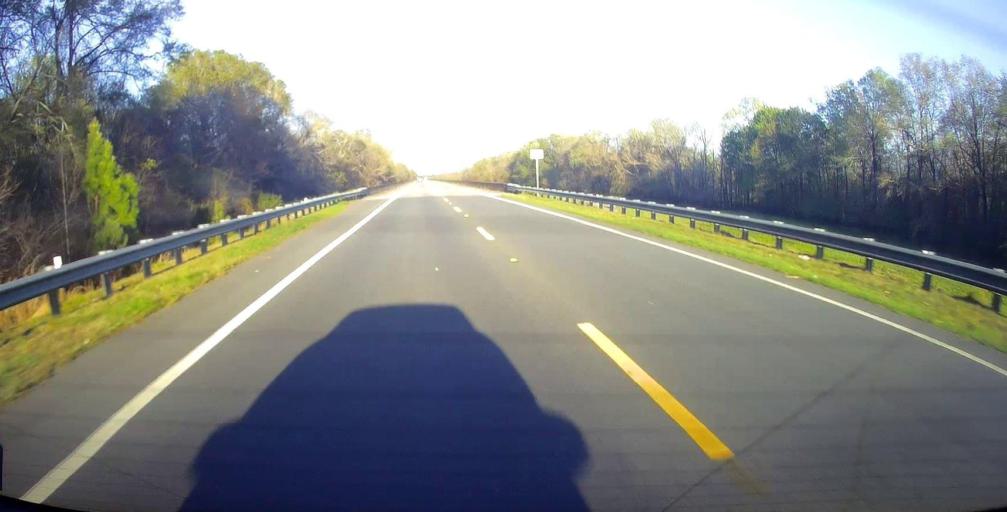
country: US
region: Georgia
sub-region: Wilcox County
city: Abbeville
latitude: 31.9950
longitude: -83.2890
